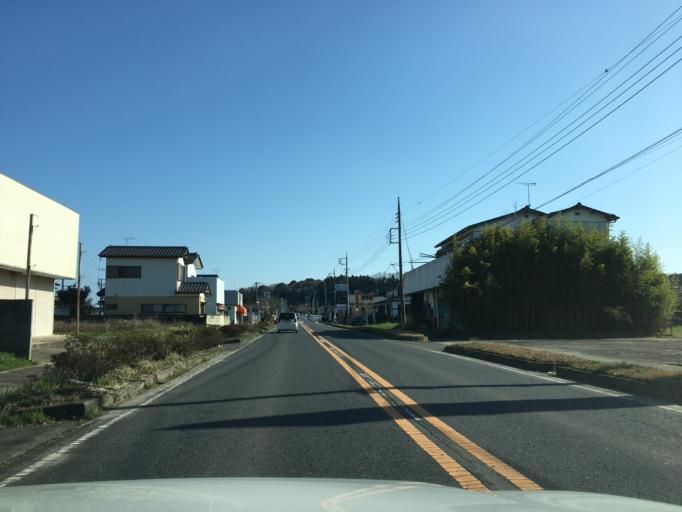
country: JP
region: Ibaraki
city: Omiya
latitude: 36.4462
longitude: 140.4106
